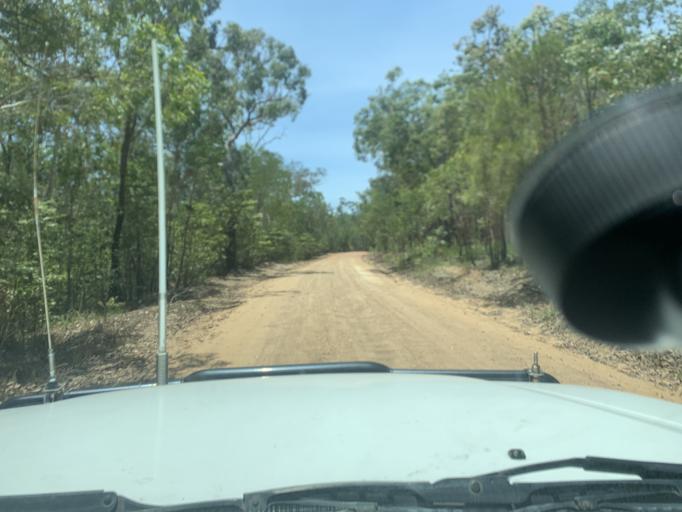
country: AU
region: Queensland
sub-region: Tablelands
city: Kuranda
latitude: -16.9184
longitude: 145.5932
